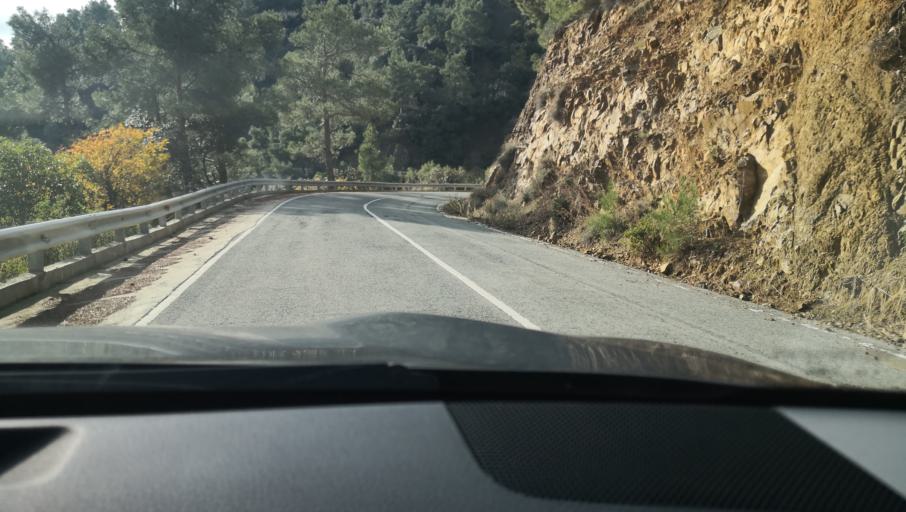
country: CY
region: Lefkosia
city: Lefka
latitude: 35.0134
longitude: 32.7308
